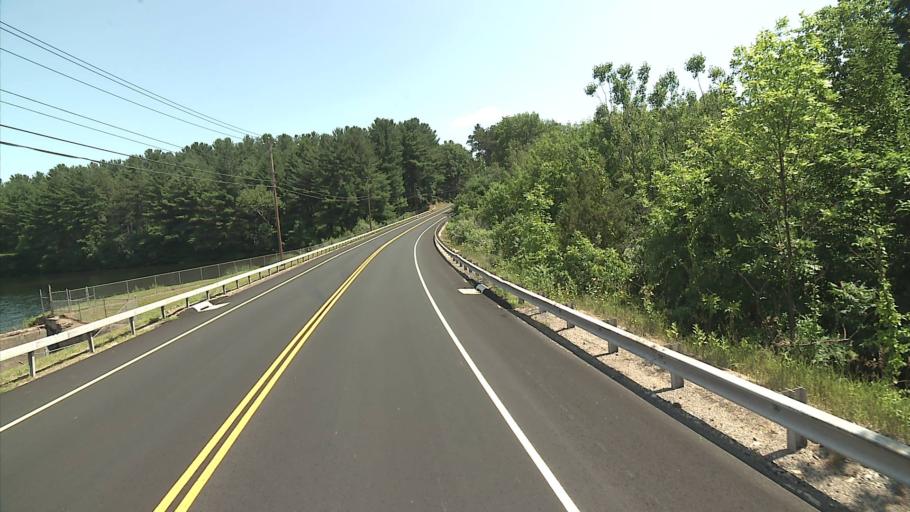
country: US
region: Connecticut
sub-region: Litchfield County
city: Winchester Center
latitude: 41.9168
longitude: -73.1058
